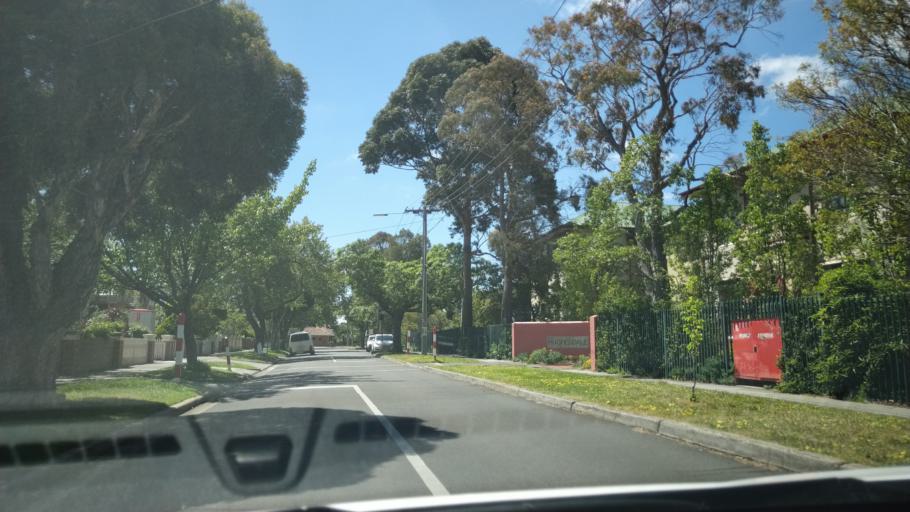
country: AU
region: Victoria
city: Hughesdale
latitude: -37.9061
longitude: 145.0774
